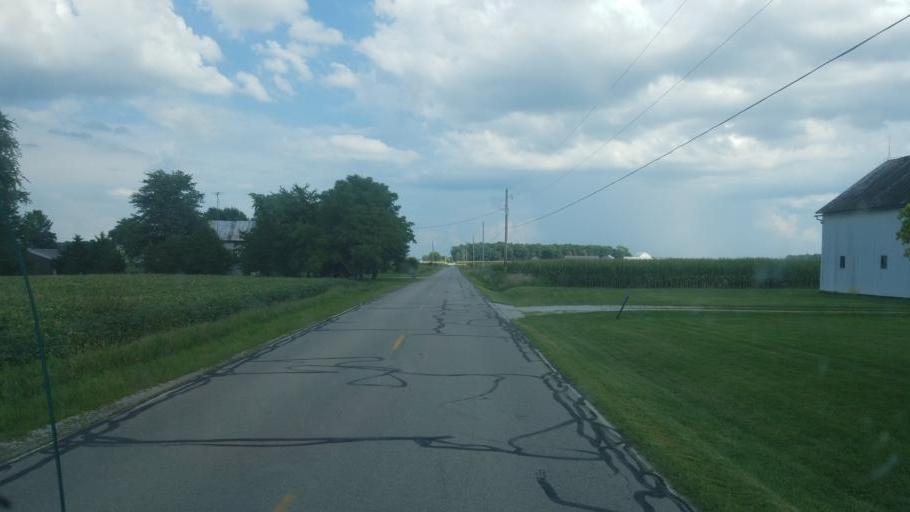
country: US
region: Ohio
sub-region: Huron County
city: Willard
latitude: 40.9819
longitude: -82.8145
